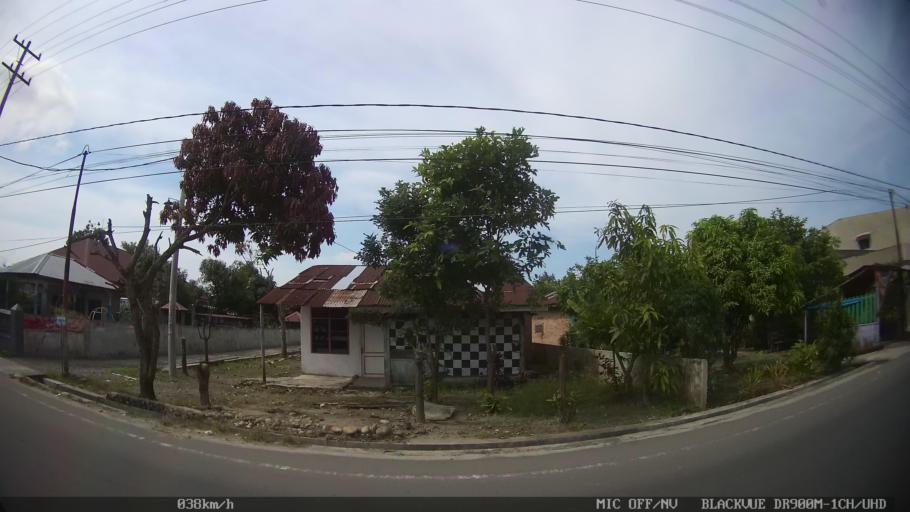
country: ID
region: North Sumatra
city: Percut
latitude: 3.6073
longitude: 98.7710
